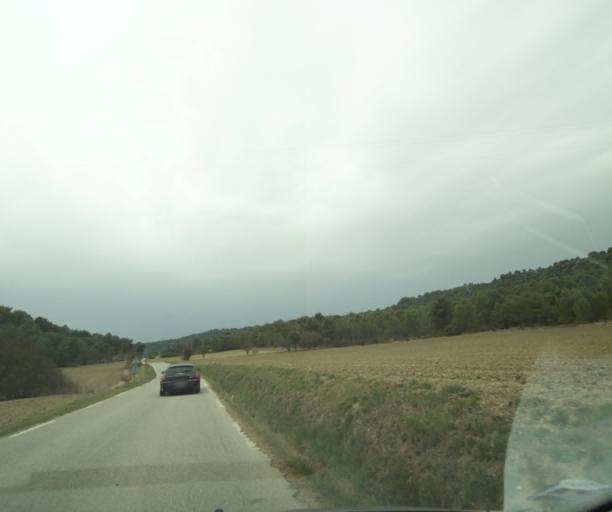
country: FR
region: Provence-Alpes-Cote d'Azur
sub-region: Departement des Bouches-du-Rhone
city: Saint-Marc-Jaumegarde
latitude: 43.5567
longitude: 5.5611
